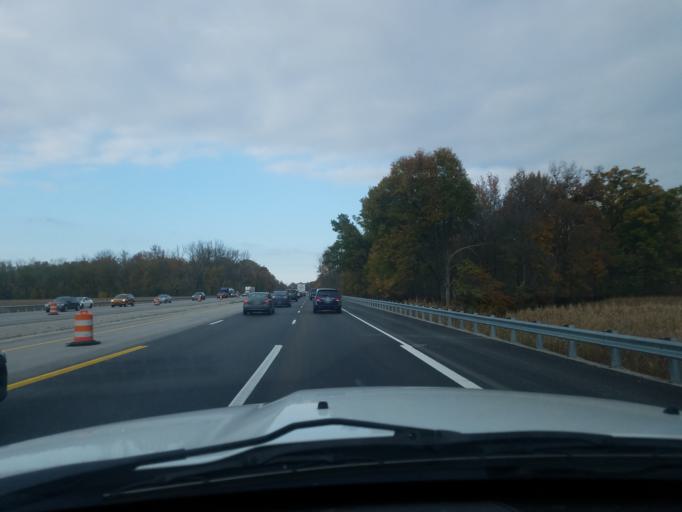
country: US
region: Indiana
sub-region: Clark County
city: Sellersburg
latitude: 38.4255
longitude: -85.7647
